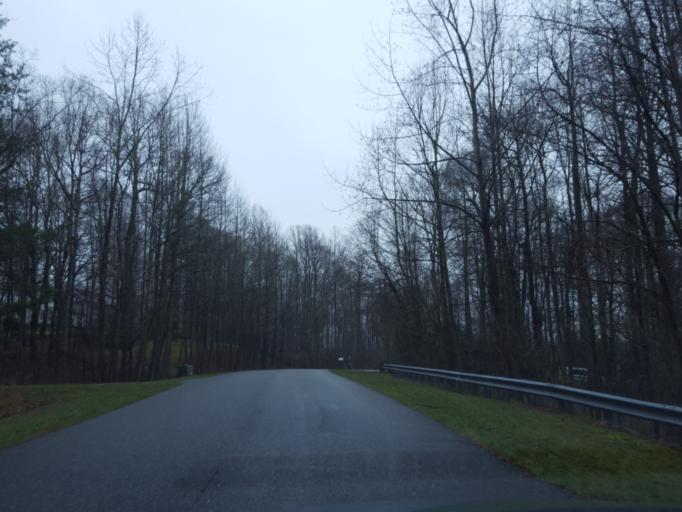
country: US
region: Maryland
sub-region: Calvert County
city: Huntingtown
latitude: 38.6092
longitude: -76.5381
